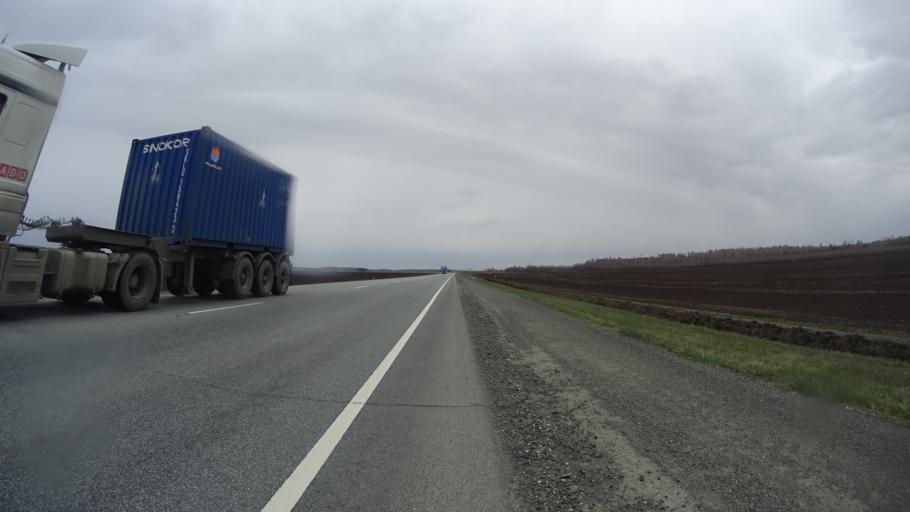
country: RU
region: Chelyabinsk
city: Krasnogorskiy
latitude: 54.5728
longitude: 61.2908
